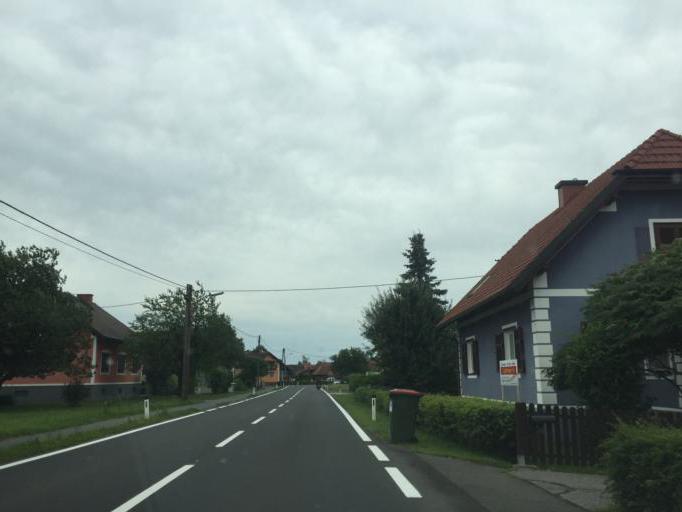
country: SI
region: Sentilj
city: Selnica ob Muri
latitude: 46.7135
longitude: 15.6911
